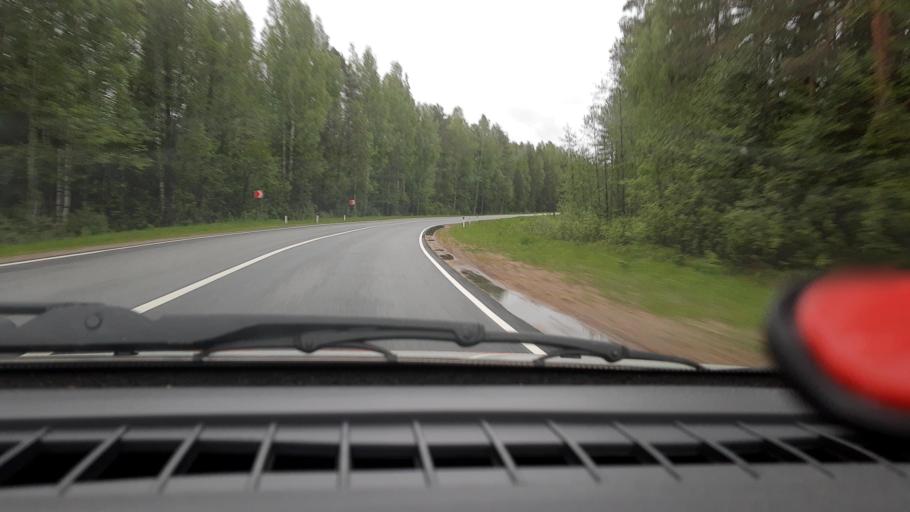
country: RU
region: Nizjnij Novgorod
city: Krasnyye Baki
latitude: 57.2216
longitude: 45.4858
